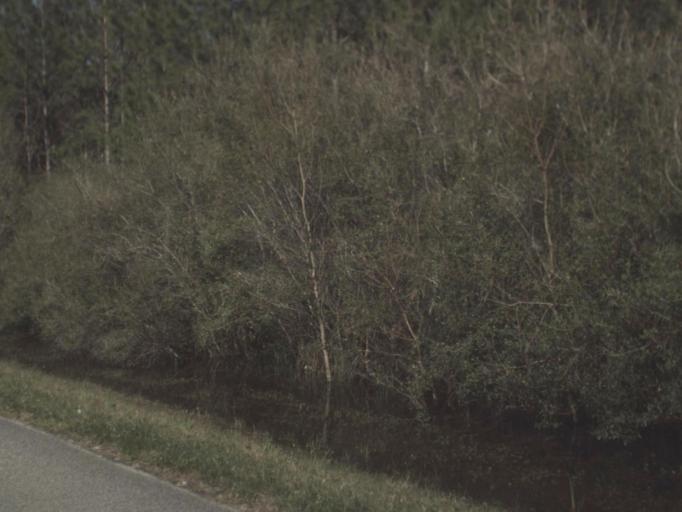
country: US
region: Florida
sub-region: Gulf County
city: Wewahitchka
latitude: 30.0124
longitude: -85.1760
